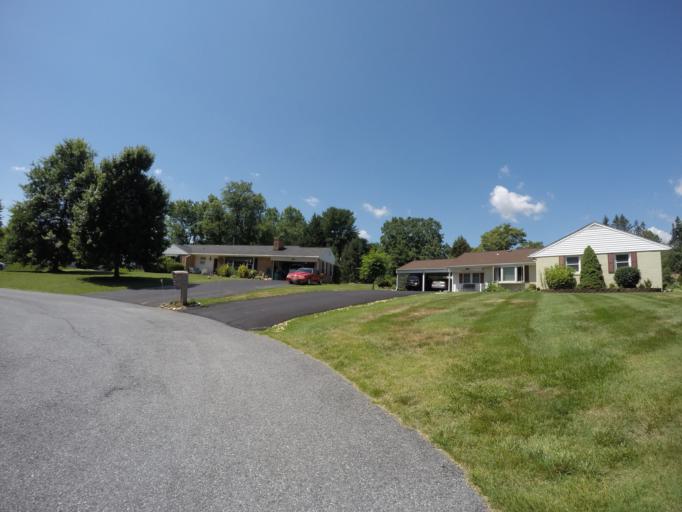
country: US
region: Maryland
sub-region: Howard County
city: Columbia
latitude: 39.2750
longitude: -76.8548
